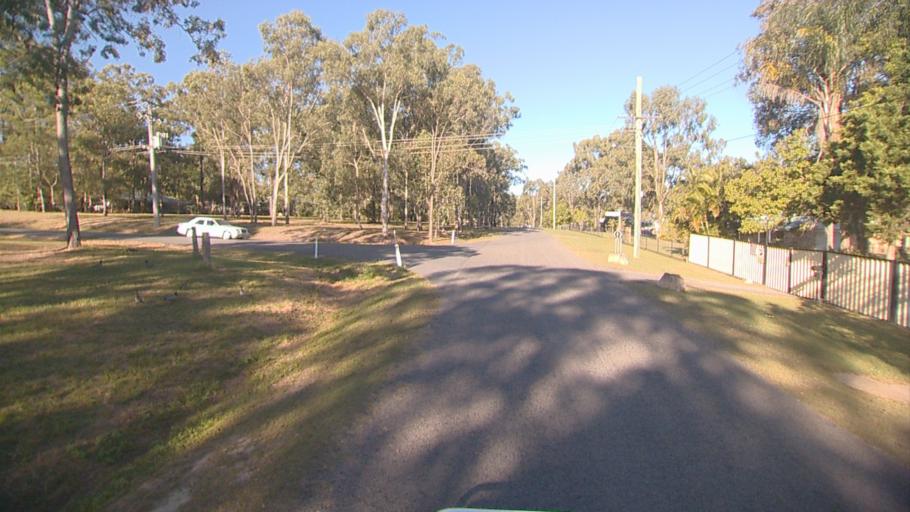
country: AU
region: Queensland
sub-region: Logan
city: Logan Reserve
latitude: -27.7452
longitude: 153.1068
